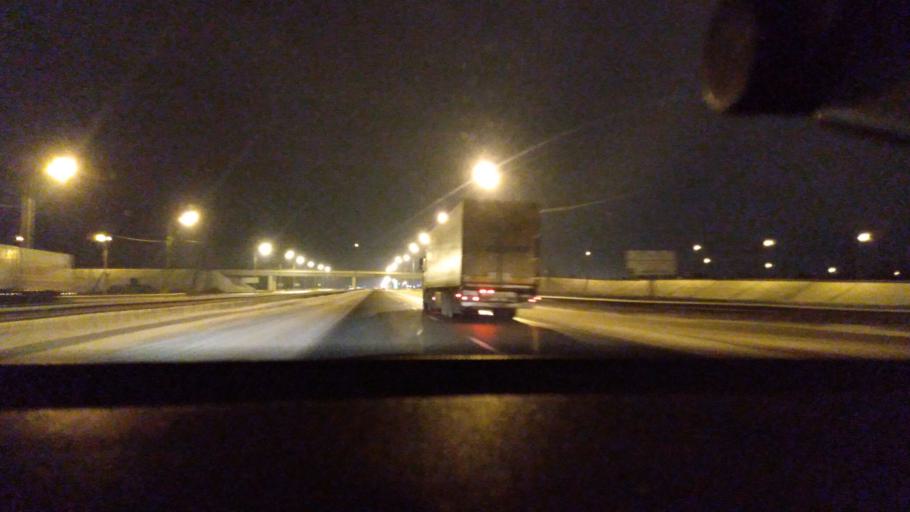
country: RU
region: Moskovskaya
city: Kolomna
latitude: 55.1218
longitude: 38.8141
